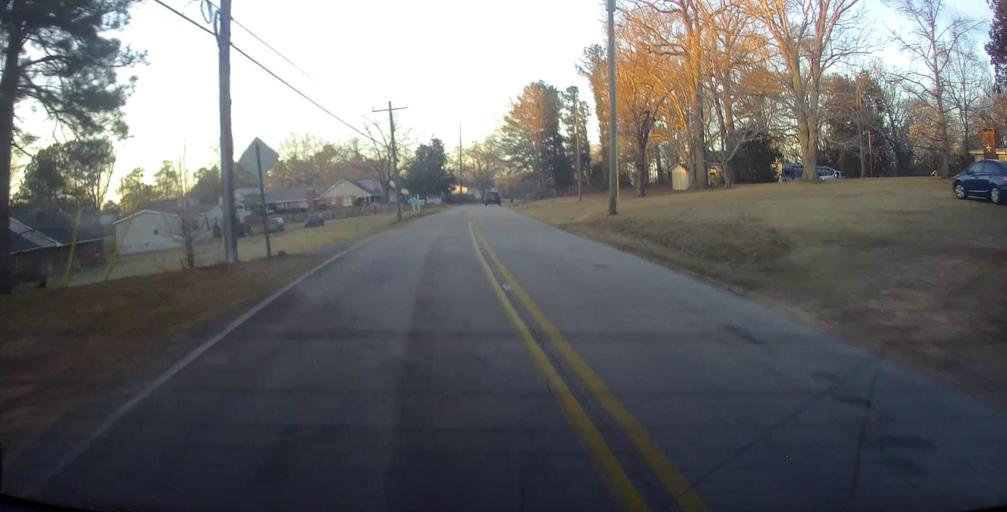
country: US
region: Georgia
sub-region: Troup County
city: La Grange
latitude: 33.0177
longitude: -85.0053
